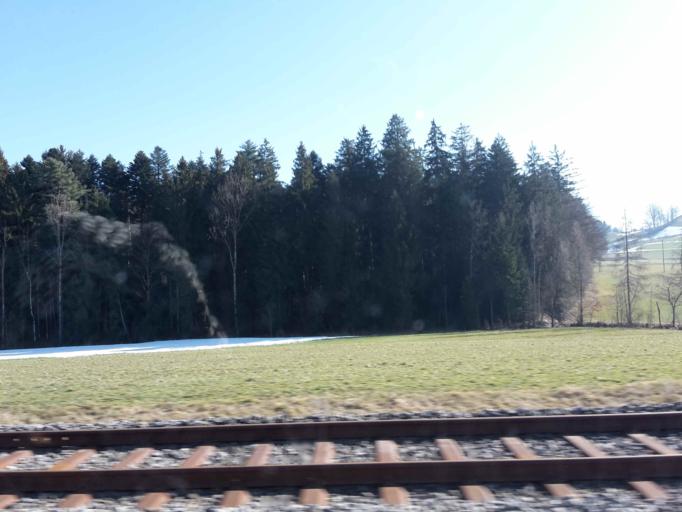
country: CH
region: Bern
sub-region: Emmental District
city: Durrenroth
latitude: 47.0853
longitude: 7.7589
